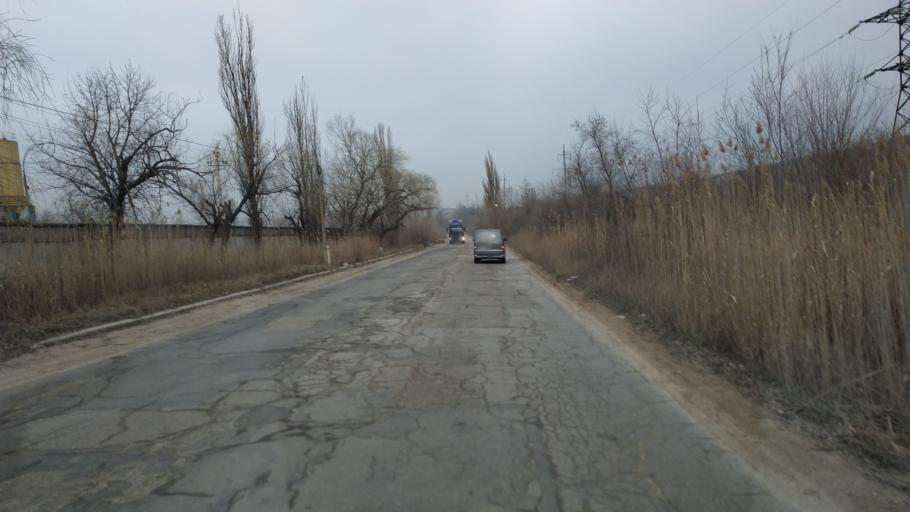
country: MD
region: Chisinau
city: Vatra
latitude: 47.0686
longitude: 28.7770
